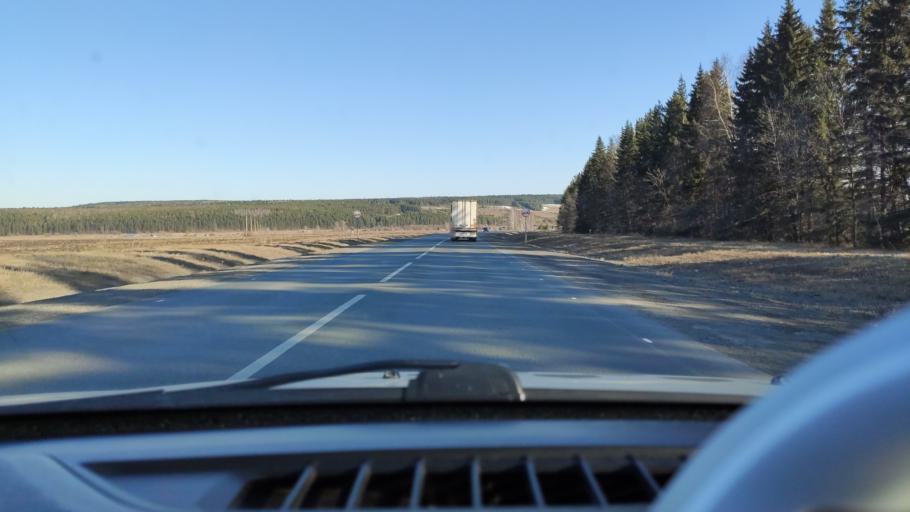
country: RU
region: Perm
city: Suksun
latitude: 57.0718
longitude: 57.4161
